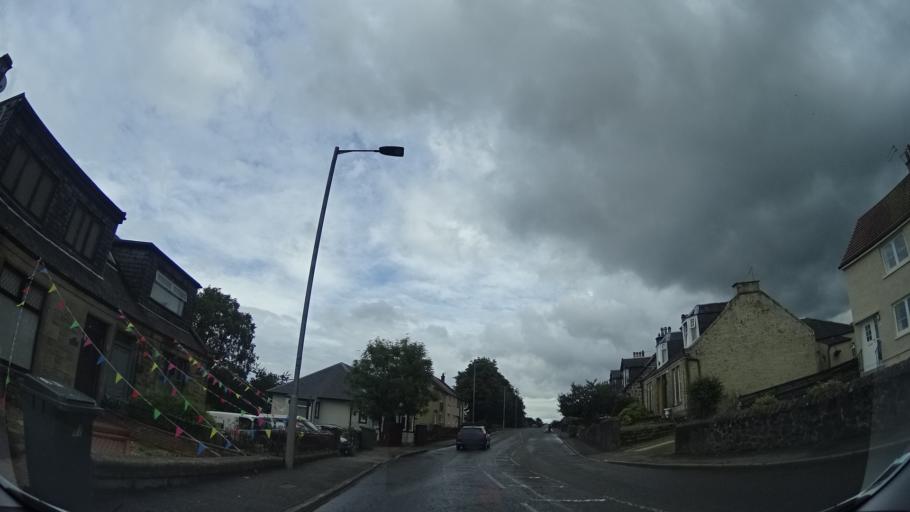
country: GB
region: Scotland
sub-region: Falkirk
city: Bonnybridge
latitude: 56.0029
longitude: -3.8816
